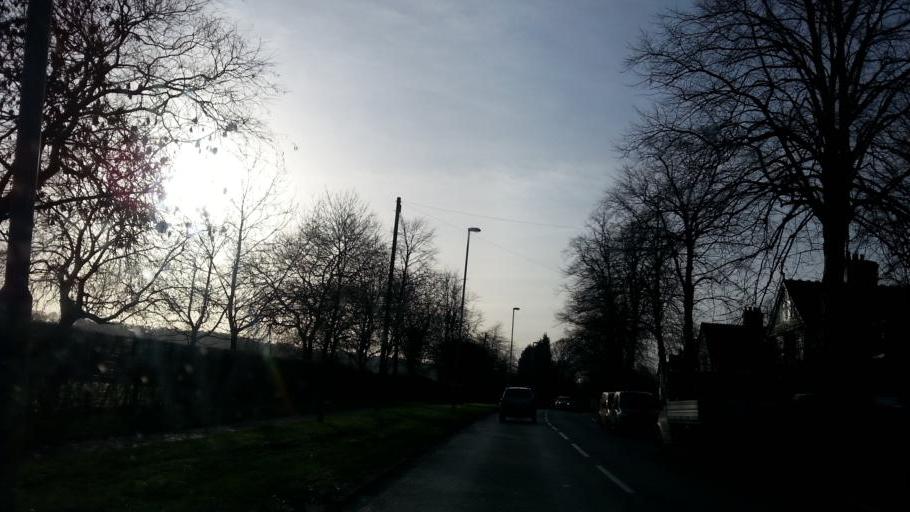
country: GB
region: England
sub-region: Staffordshire
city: Biddulph
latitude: 53.0694
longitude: -2.1183
